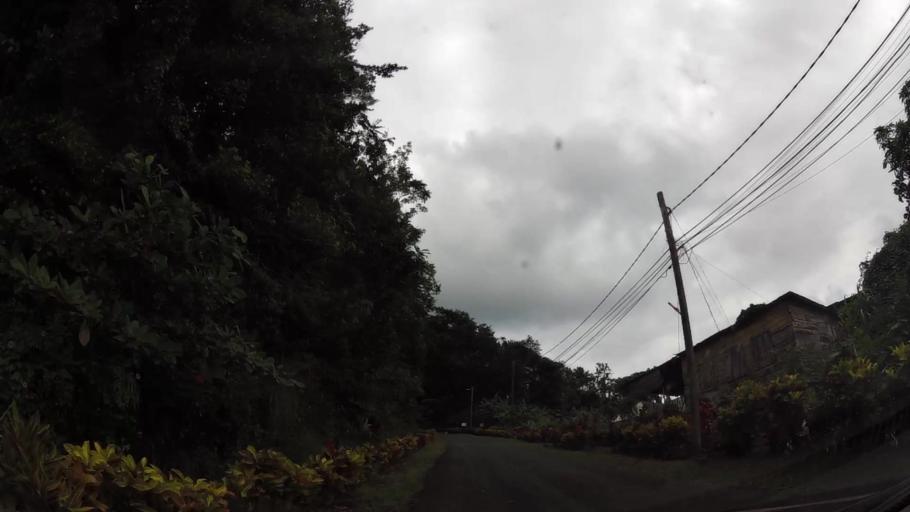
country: DM
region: Saint David
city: Castle Bruce
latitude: 15.4392
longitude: -61.2592
